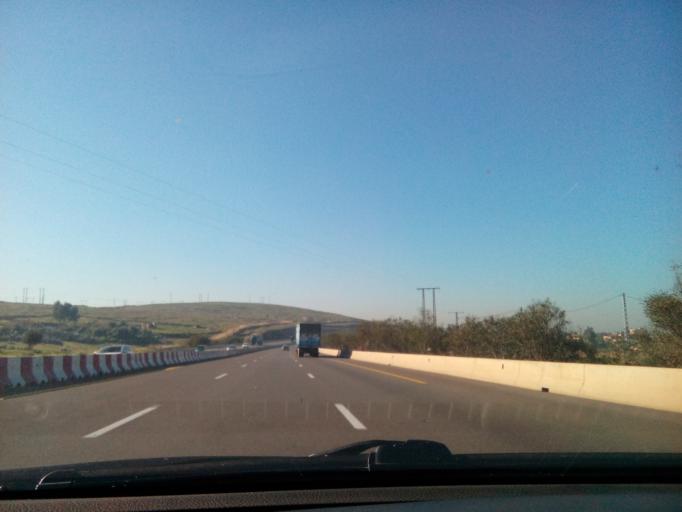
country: DZ
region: Chlef
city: Oued Sly
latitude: 36.0707
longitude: 1.1693
